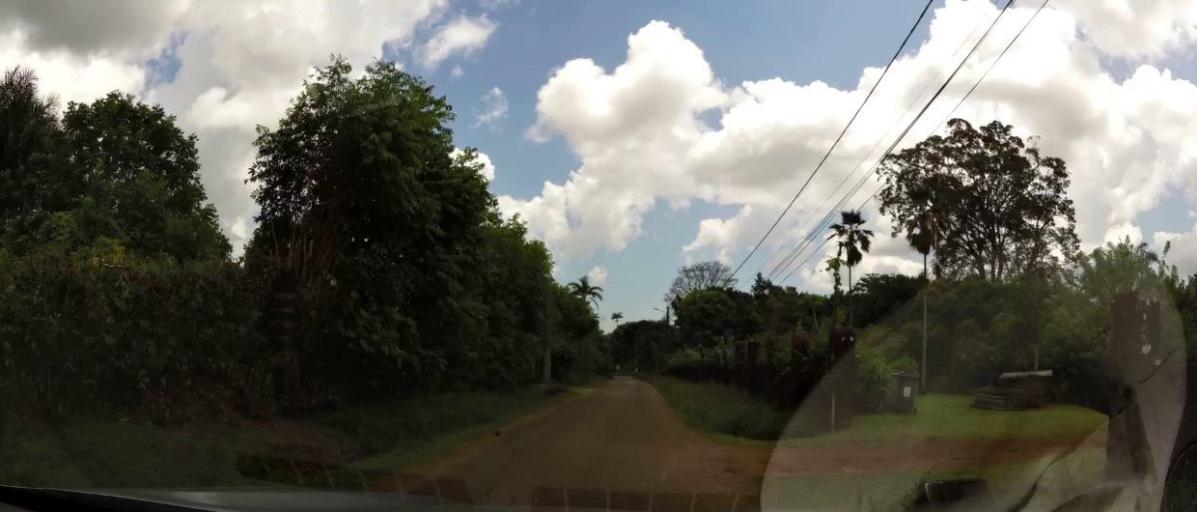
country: GF
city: Macouria
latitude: 4.8803
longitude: -52.3599
